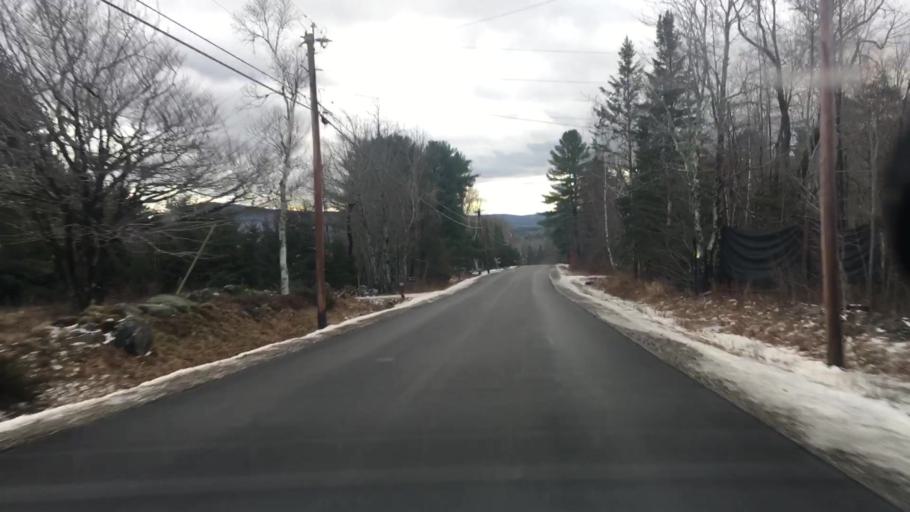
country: US
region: Maine
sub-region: Hancock County
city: Dedham
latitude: 44.6566
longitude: -68.7043
